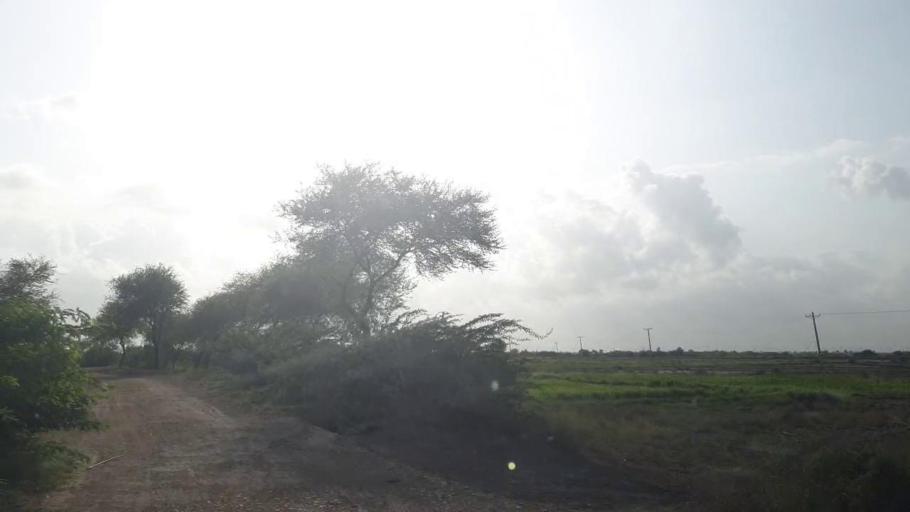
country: PK
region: Sindh
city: Kadhan
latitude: 24.6276
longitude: 69.0873
